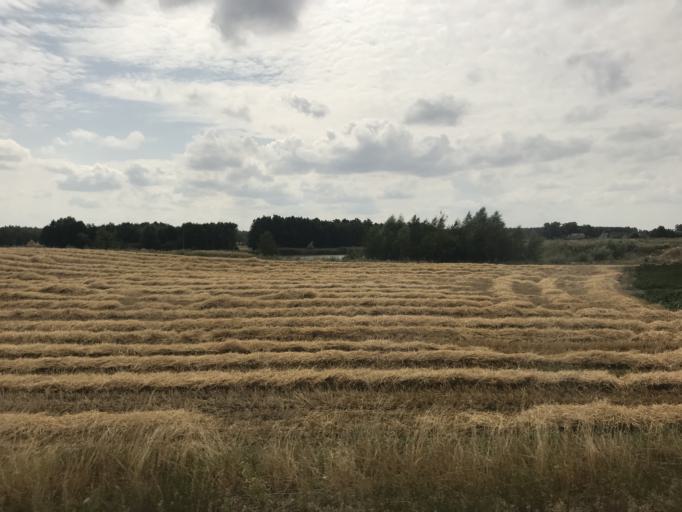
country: PL
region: Greater Poland Voivodeship
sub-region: Powiat gnieznienski
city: Trzemeszno
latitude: 52.5452
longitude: 17.7382
